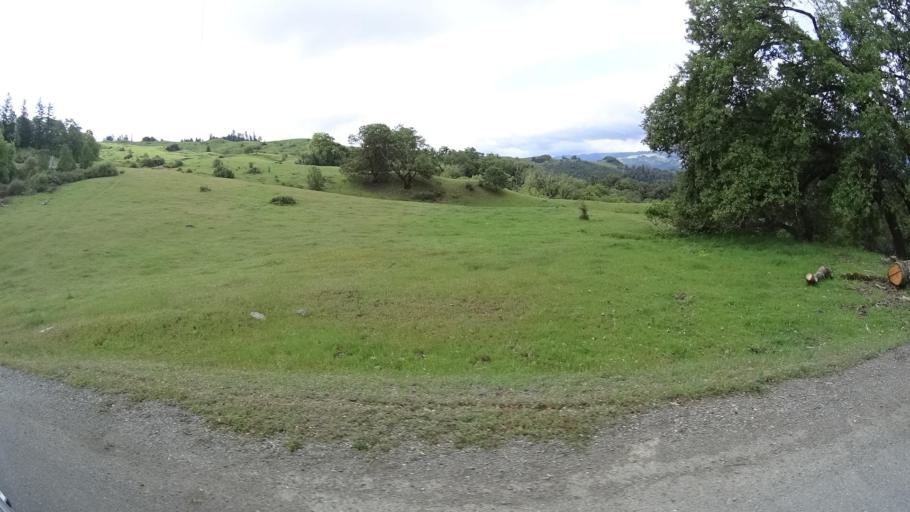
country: US
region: California
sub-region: Humboldt County
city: Redway
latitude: 40.1819
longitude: -123.5724
